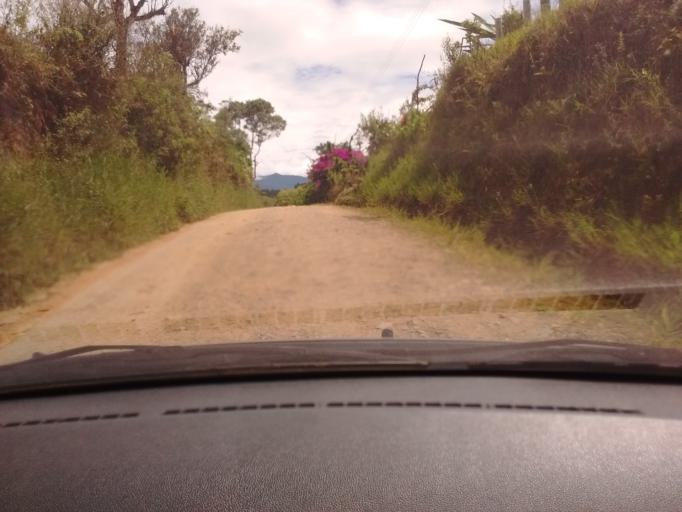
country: CO
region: Cauca
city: El Tambo
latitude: 2.4528
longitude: -76.8249
